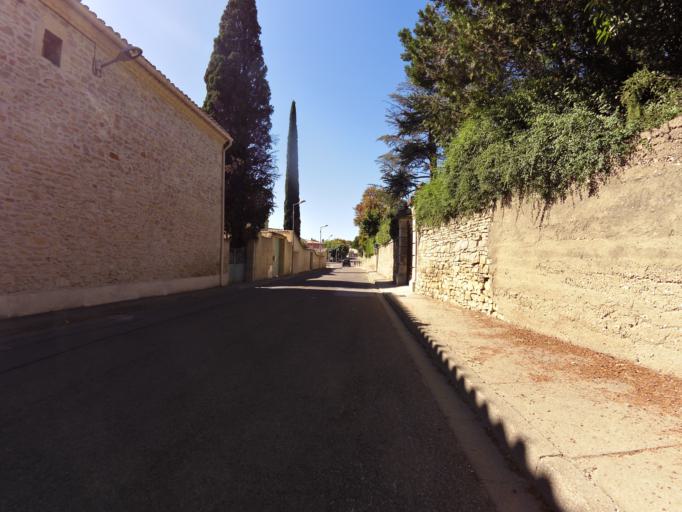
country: FR
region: Languedoc-Roussillon
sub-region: Departement du Gard
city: Vergeze
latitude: 43.7425
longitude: 4.2255
